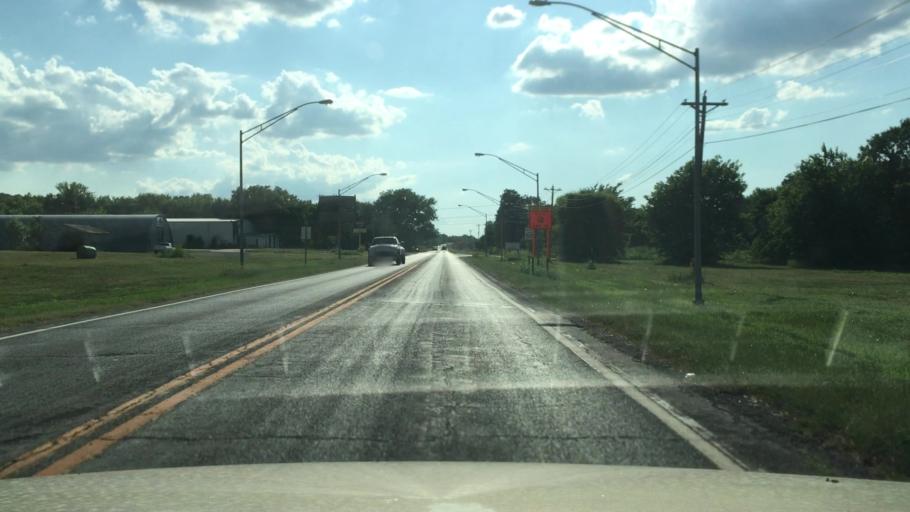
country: US
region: Oklahoma
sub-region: Cherokee County
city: Tahlequah
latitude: 35.9202
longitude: -95.0094
